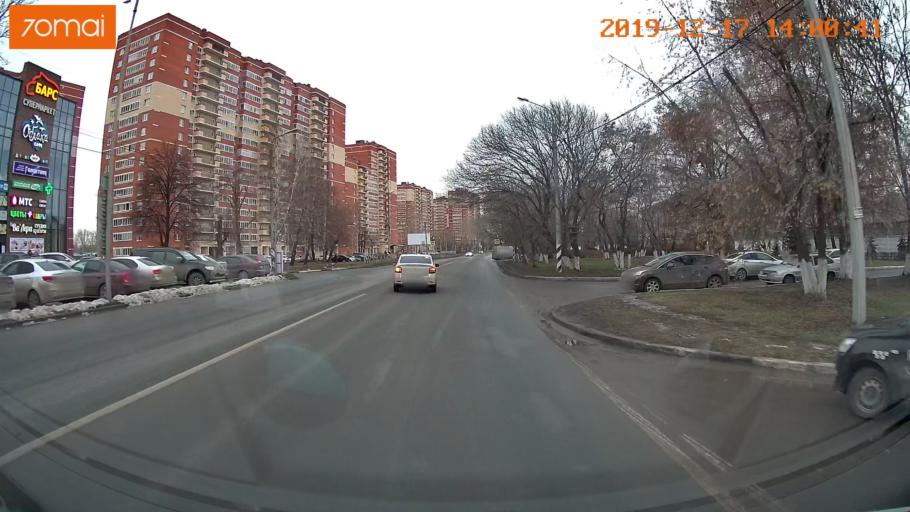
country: RU
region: Rjazan
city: Ryazan'
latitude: 54.6185
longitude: 39.6694
